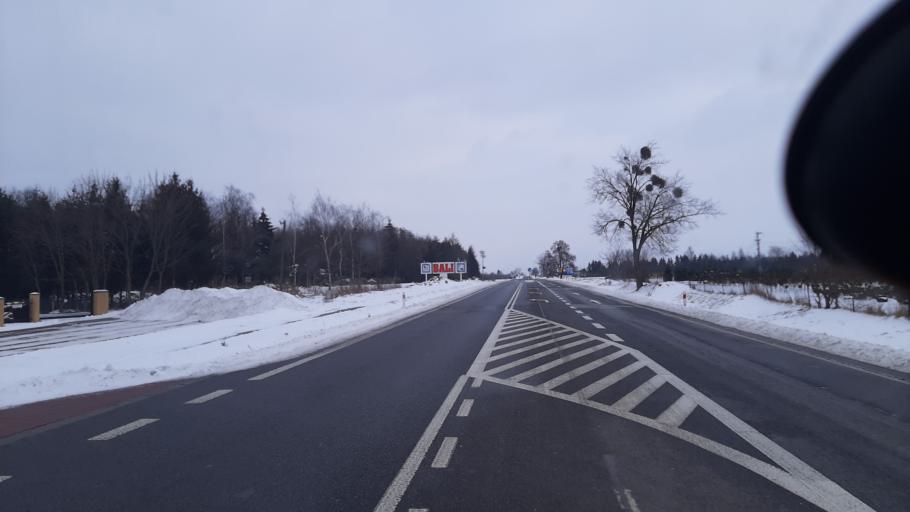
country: PL
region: Lublin Voivodeship
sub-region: Powiat pulawski
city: Kurow
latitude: 51.3854
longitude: 22.2110
